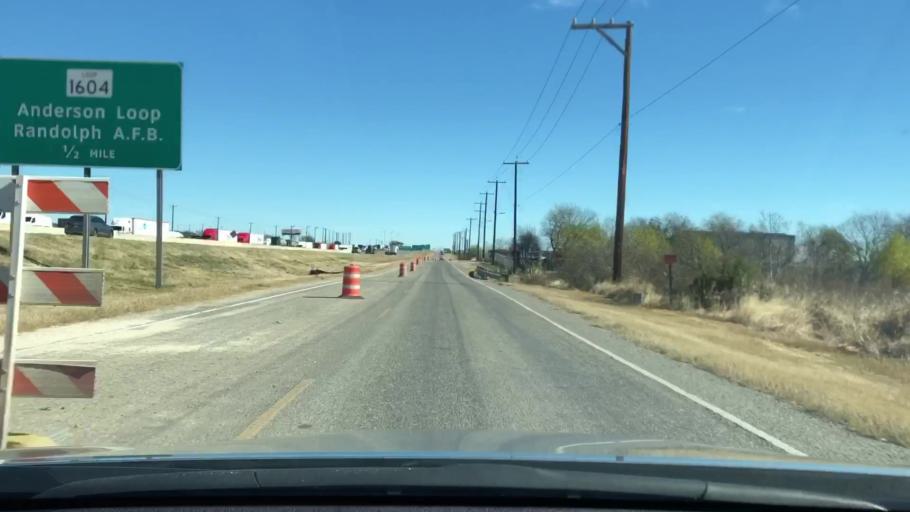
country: US
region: Texas
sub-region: Bexar County
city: Converse
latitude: 29.4622
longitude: -98.3031
